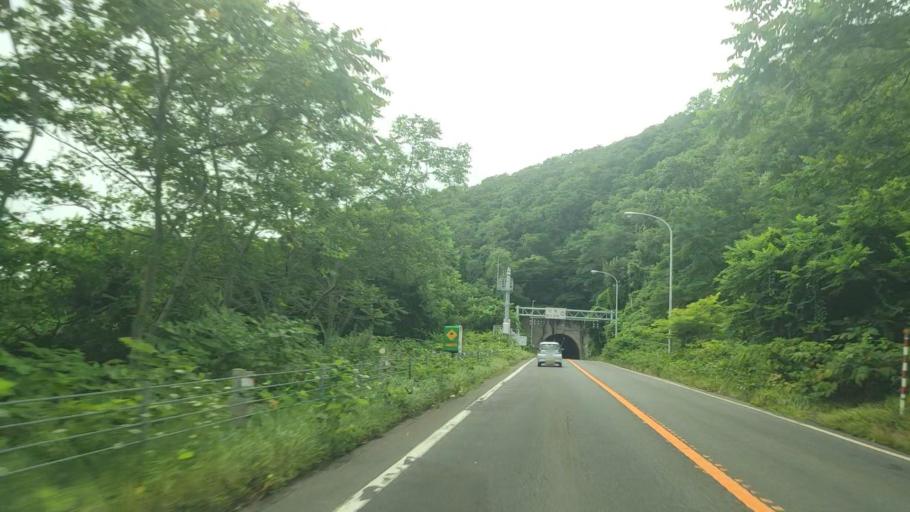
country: JP
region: Hokkaido
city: Date
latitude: 42.5626
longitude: 140.7434
